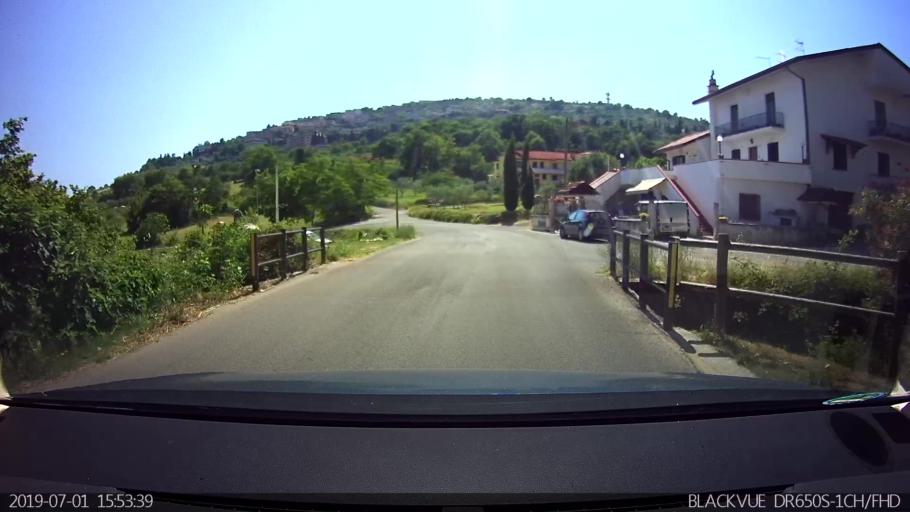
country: IT
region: Latium
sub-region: Provincia di Frosinone
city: Veroli
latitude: 41.6997
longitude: 13.4273
